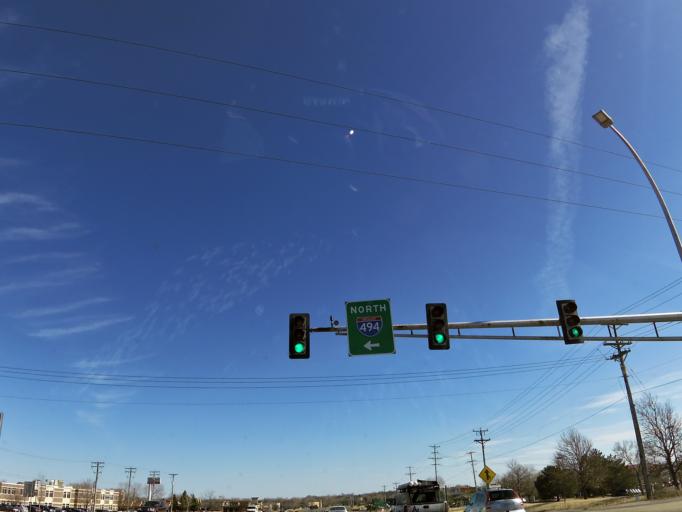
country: US
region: Minnesota
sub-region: Hennepin County
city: Plymouth
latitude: 45.0103
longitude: -93.4559
